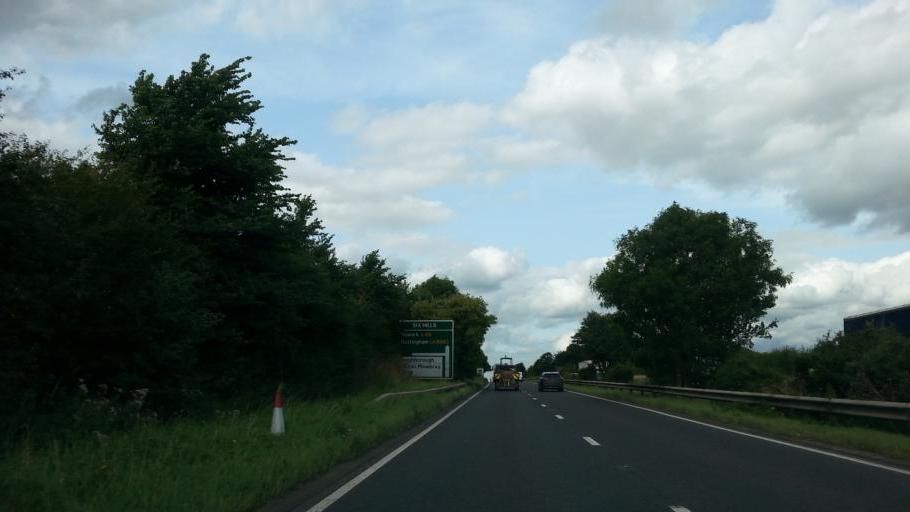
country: GB
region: England
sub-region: Leicestershire
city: Grimston
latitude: 52.7778
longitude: -1.0484
